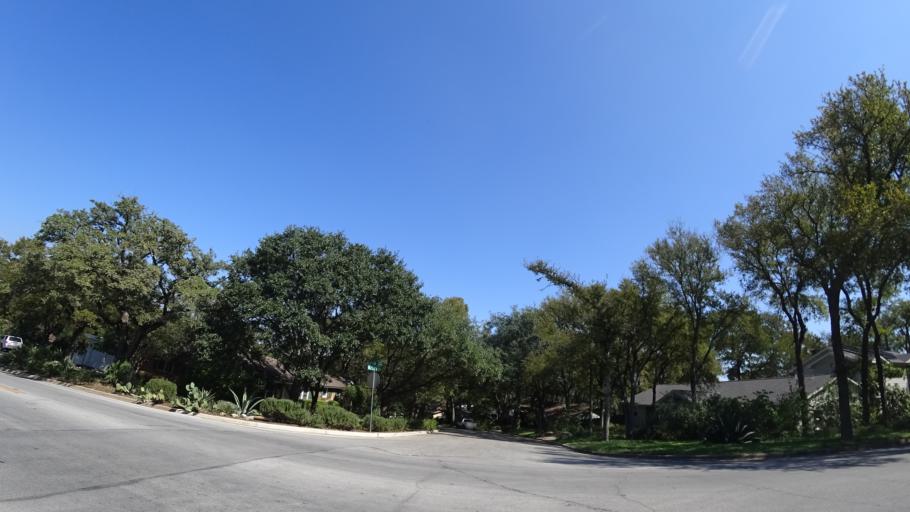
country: US
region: Texas
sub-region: Travis County
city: Rollingwood
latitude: 30.2509
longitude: -97.7856
